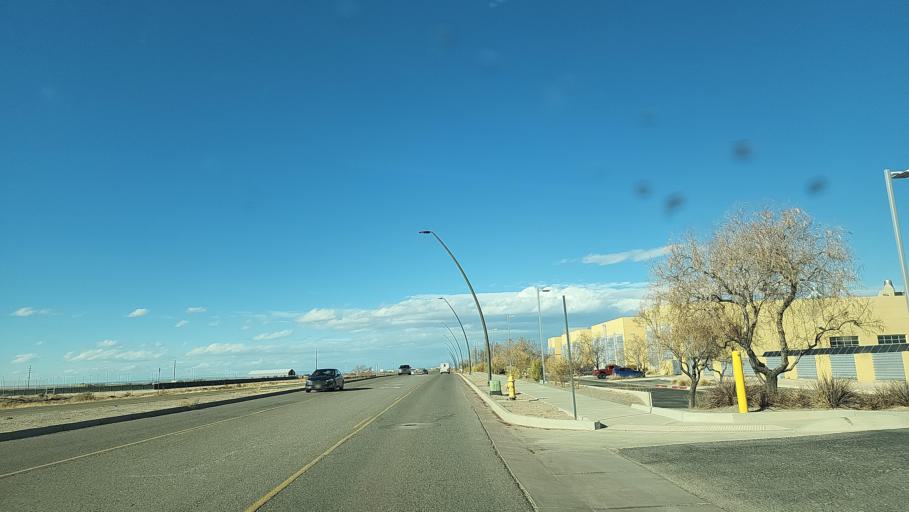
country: US
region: New Mexico
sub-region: Bernalillo County
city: South Valley
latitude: 34.9951
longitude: -106.6217
